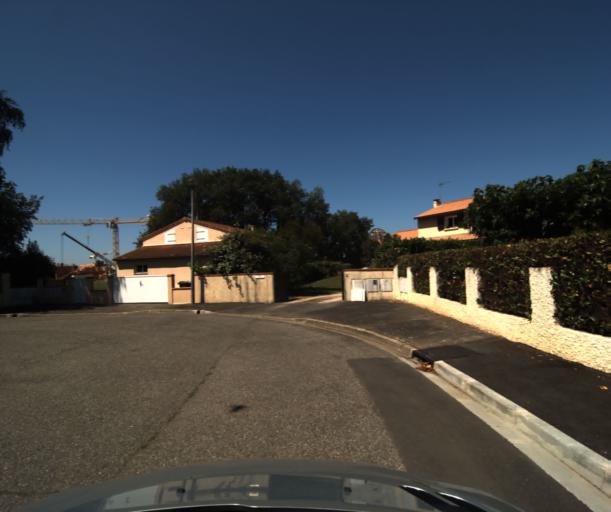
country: FR
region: Midi-Pyrenees
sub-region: Departement de la Haute-Garonne
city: Roquettes
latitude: 43.4955
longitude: 1.3705
